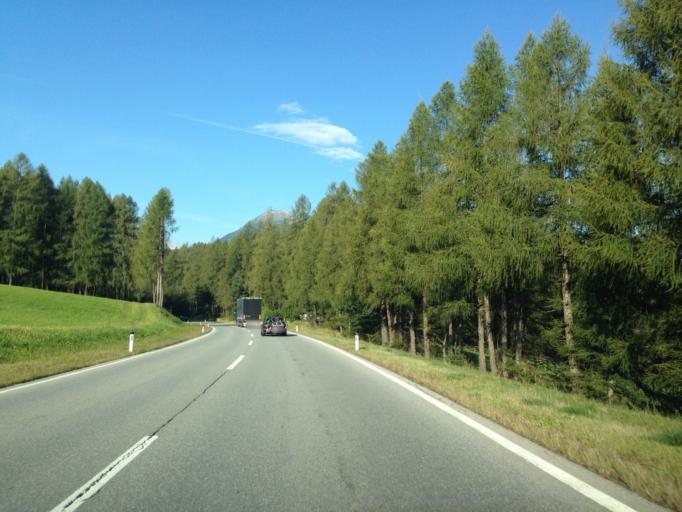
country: AT
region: Tyrol
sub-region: Politischer Bezirk Imst
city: Nassereith
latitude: 47.3084
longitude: 10.8787
